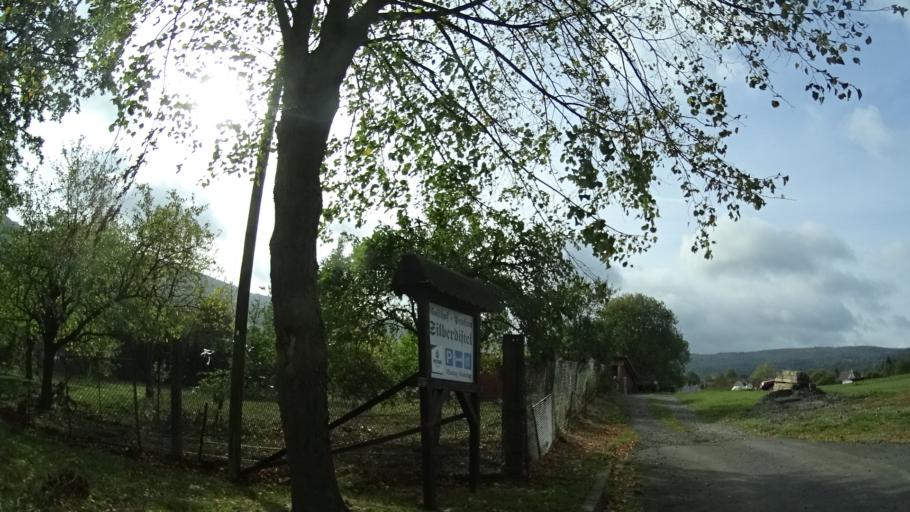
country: DE
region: Thuringia
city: Oberweid
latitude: 50.5933
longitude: 10.0621
